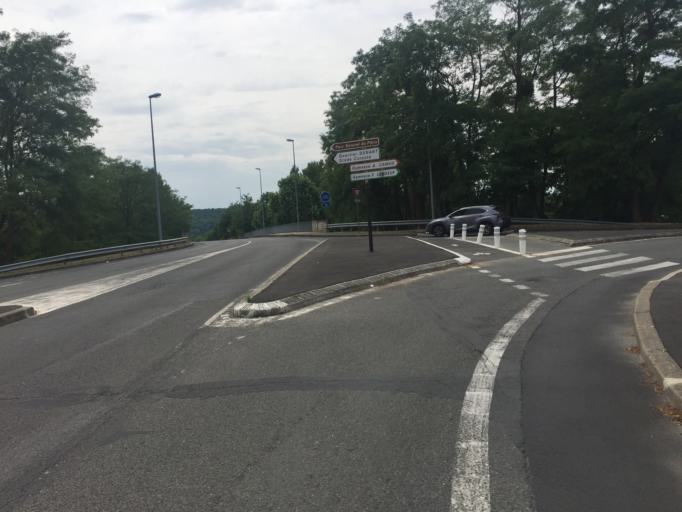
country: FR
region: Ile-de-France
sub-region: Departement de Seine-et-Marne
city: Nanteuil-les-Meaux
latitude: 48.9474
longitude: 2.9104
